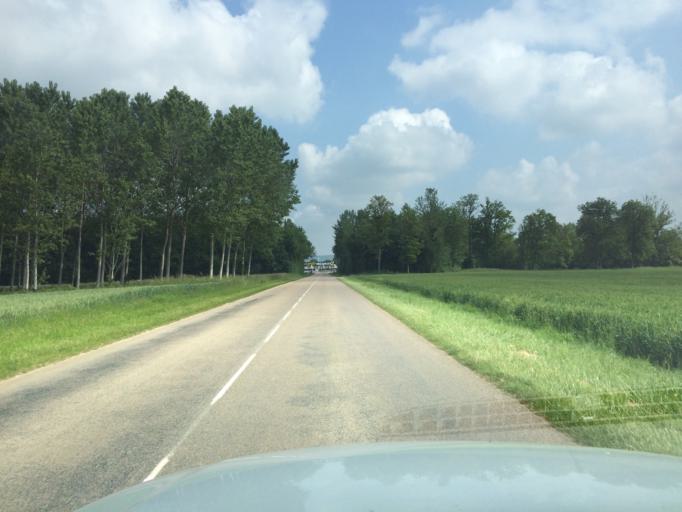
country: FR
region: Bourgogne
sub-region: Departement de l'Yonne
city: Laroche-Saint-Cydroine
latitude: 47.9537
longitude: 3.4473
